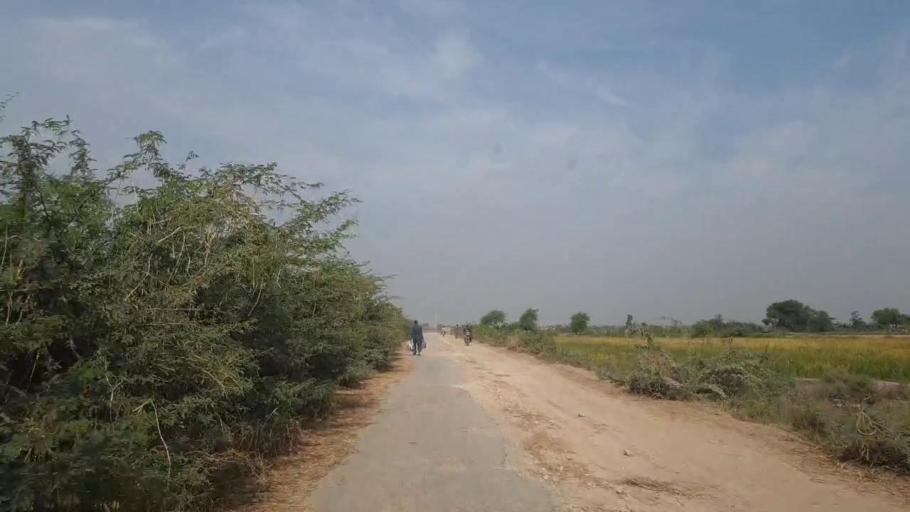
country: PK
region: Sindh
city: Tando Bago
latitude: 24.9021
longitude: 68.9976
